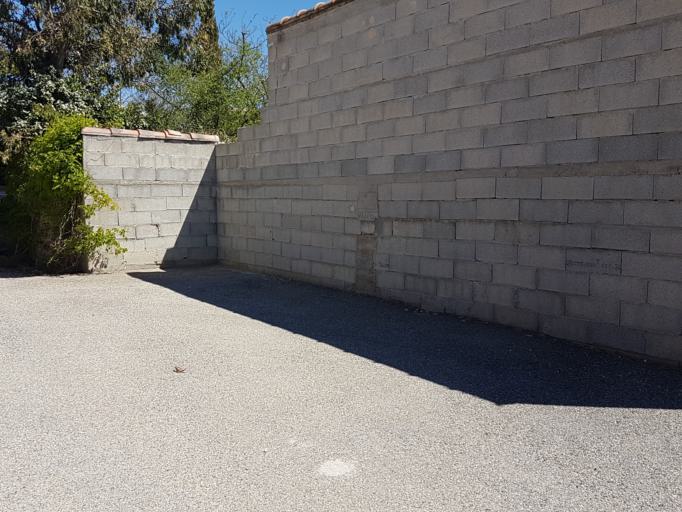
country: FR
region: Provence-Alpes-Cote d'Azur
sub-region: Departement du Vaucluse
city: Sorgues
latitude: 44.0354
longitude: 4.8672
